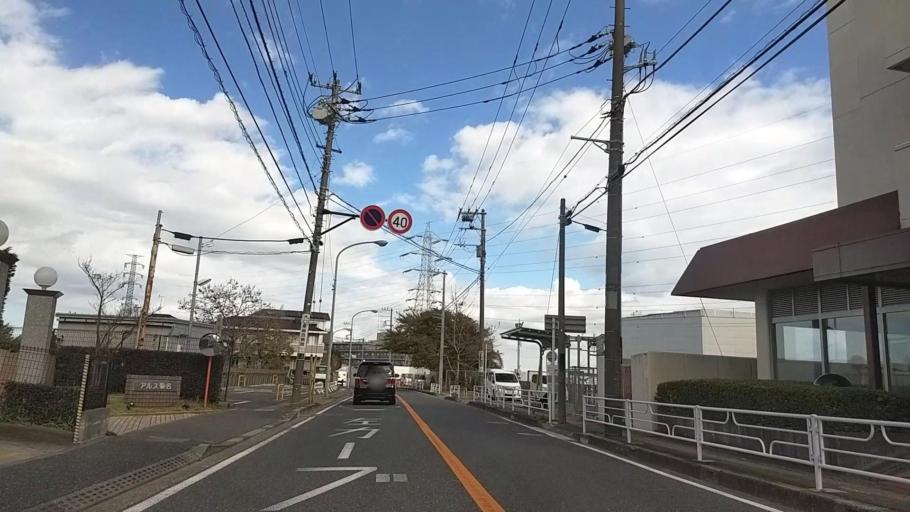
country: JP
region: Kanagawa
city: Yokohama
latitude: 35.5060
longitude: 139.6389
